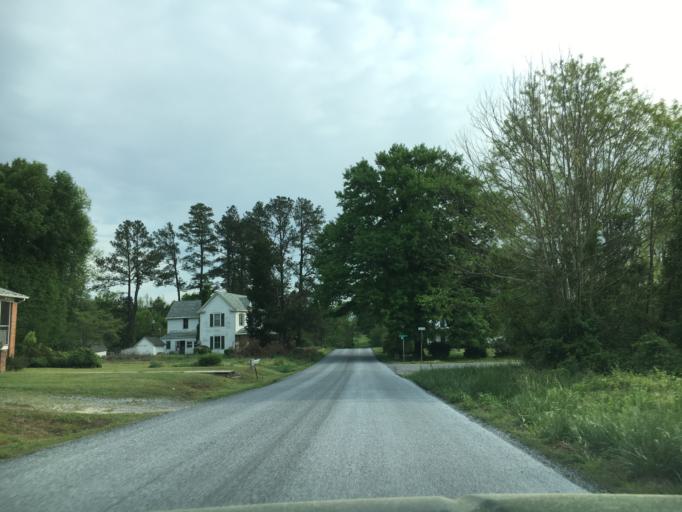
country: US
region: Virginia
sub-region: Campbell County
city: Brookneal
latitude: 36.9348
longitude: -78.9475
